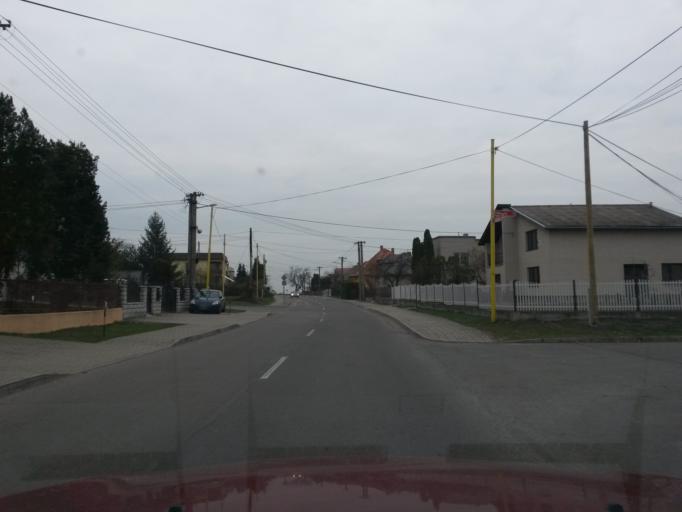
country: SK
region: Kosicky
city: Secovce
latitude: 48.7051
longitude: 21.6540
